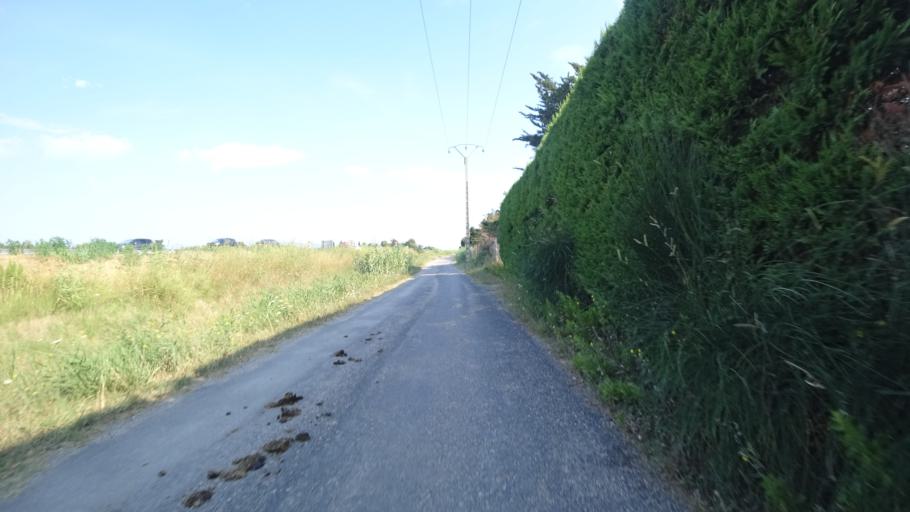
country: FR
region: Languedoc-Roussillon
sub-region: Departement des Pyrenees-Orientales
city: Le Barcares
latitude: 42.7759
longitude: 3.0165
